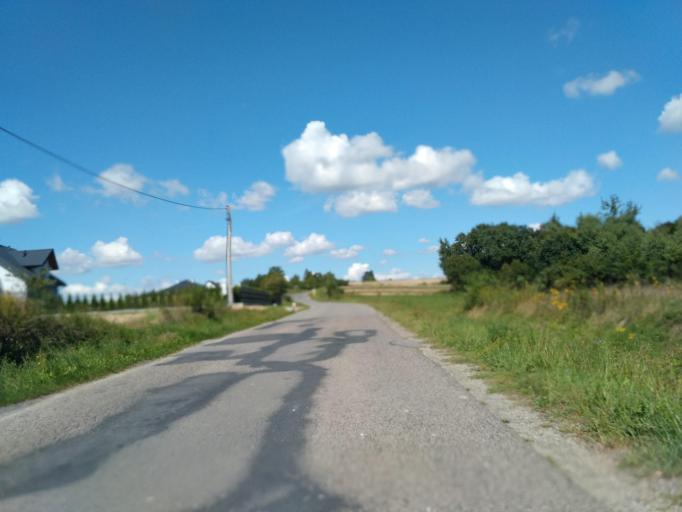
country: PL
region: Subcarpathian Voivodeship
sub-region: Powiat jasielski
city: Skolyszyn
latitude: 49.8029
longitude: 21.3137
